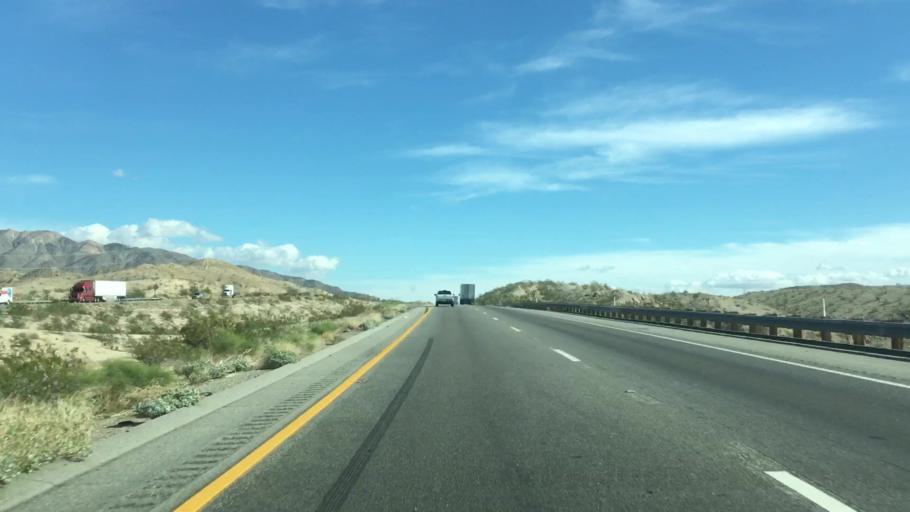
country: US
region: California
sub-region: Riverside County
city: Mecca
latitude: 33.6791
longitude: -115.9935
